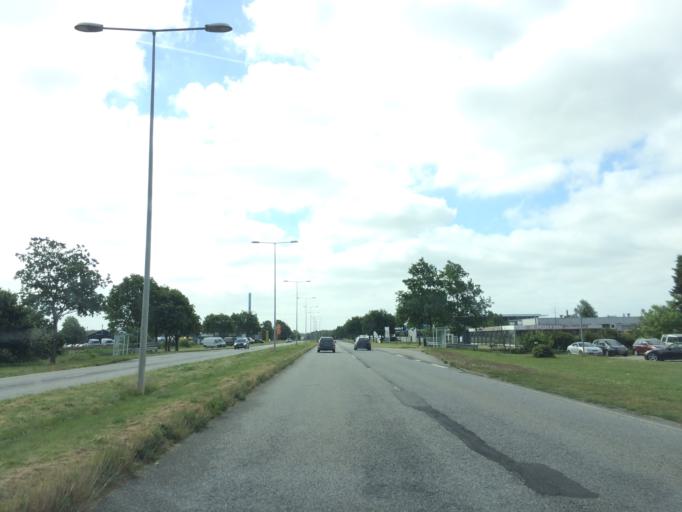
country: DK
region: Central Jutland
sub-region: Herning Kommune
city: Snejbjerg
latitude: 56.1524
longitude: 8.9322
